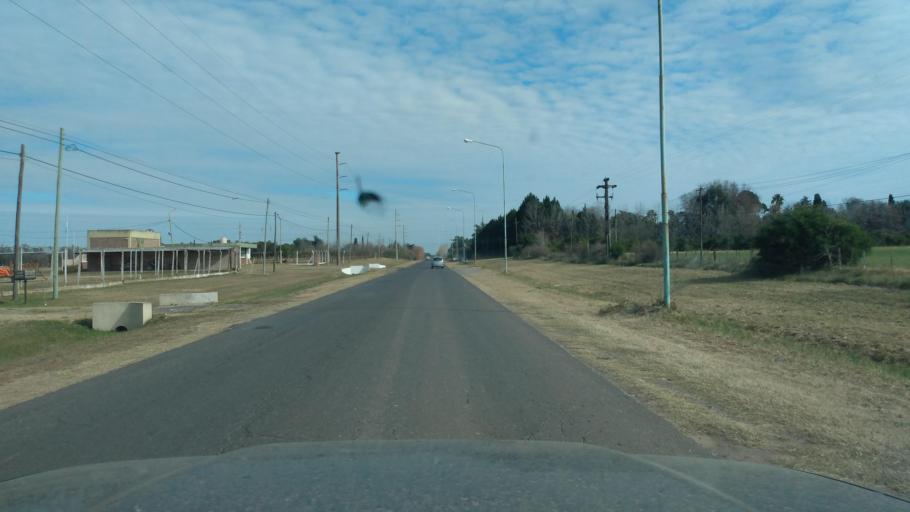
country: AR
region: Buenos Aires
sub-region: Partido de Lujan
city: Lujan
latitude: -34.5688
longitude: -59.1502
